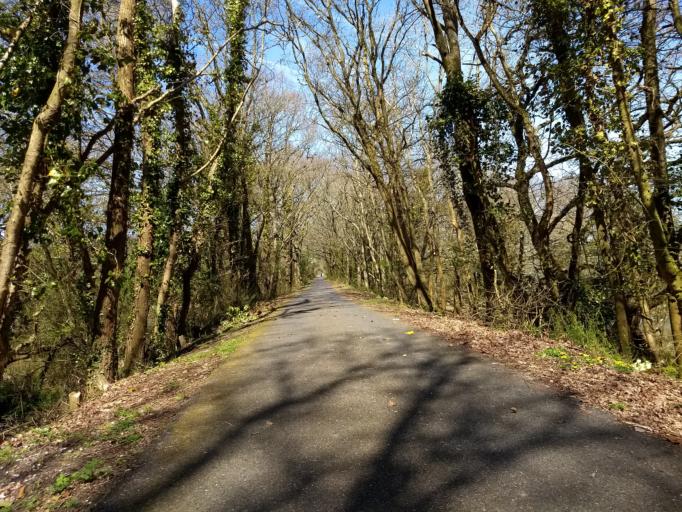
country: GB
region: England
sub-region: Isle of Wight
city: East Cowes
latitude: 50.7367
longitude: -1.2895
